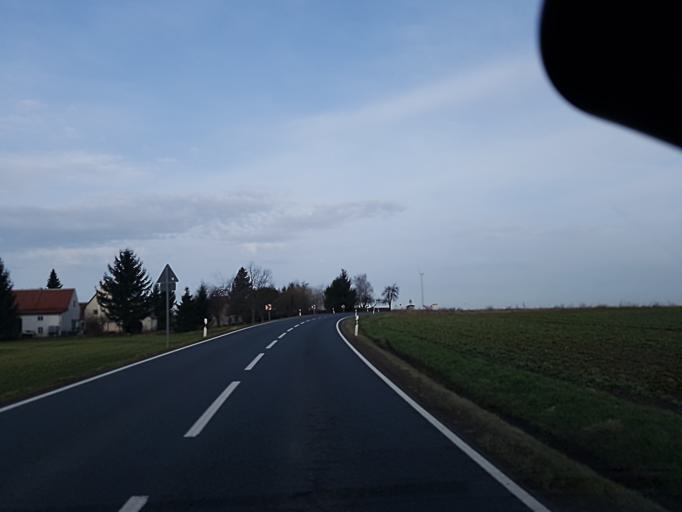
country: DE
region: Saxony
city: Grossweitzschen
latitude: 51.1774
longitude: 13.0285
